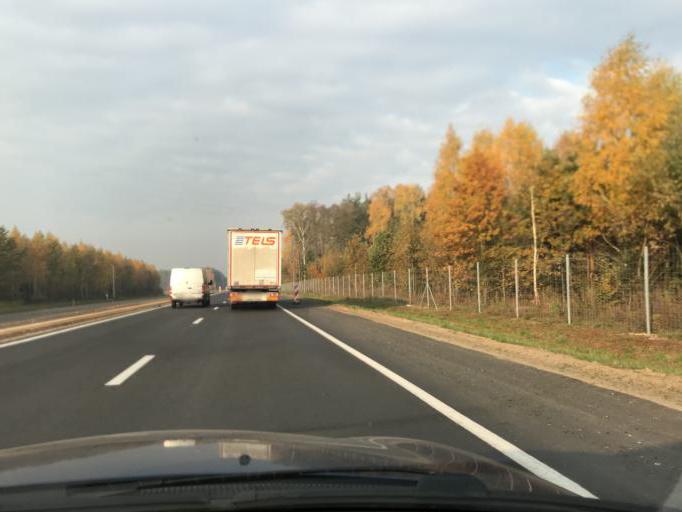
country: BY
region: Grodnenskaya
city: Lida
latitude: 53.8290
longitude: 25.3999
